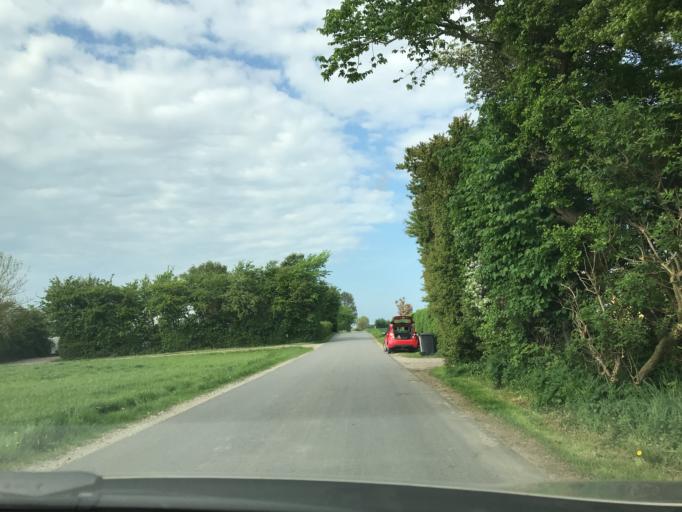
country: DK
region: South Denmark
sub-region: Middelfart Kommune
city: Norre Aby
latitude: 55.3710
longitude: 9.8442
